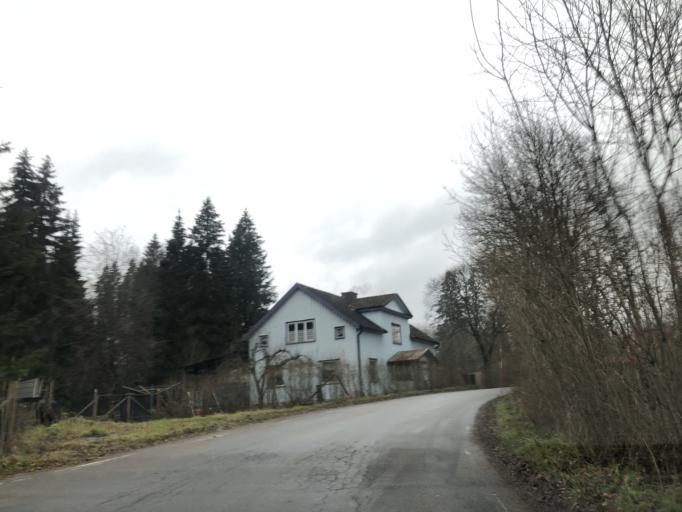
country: SE
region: Vaestra Goetaland
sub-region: Ulricehamns Kommun
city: Ulricehamn
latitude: 57.8771
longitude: 13.5304
